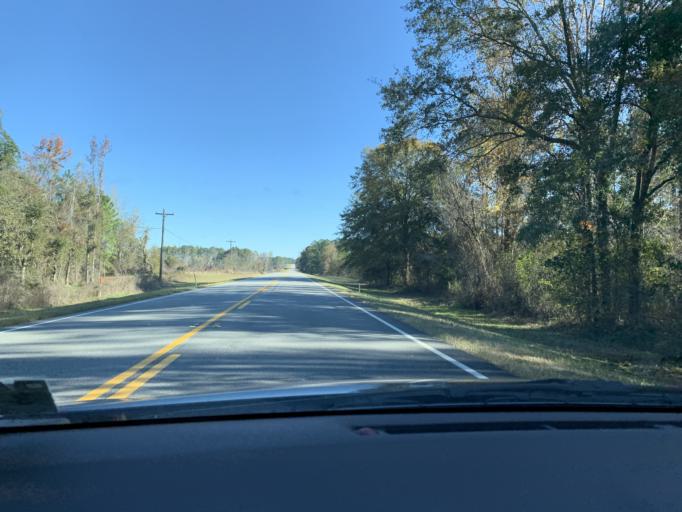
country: US
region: Georgia
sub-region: Ben Hill County
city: Fitzgerald
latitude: 31.7696
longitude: -83.1012
